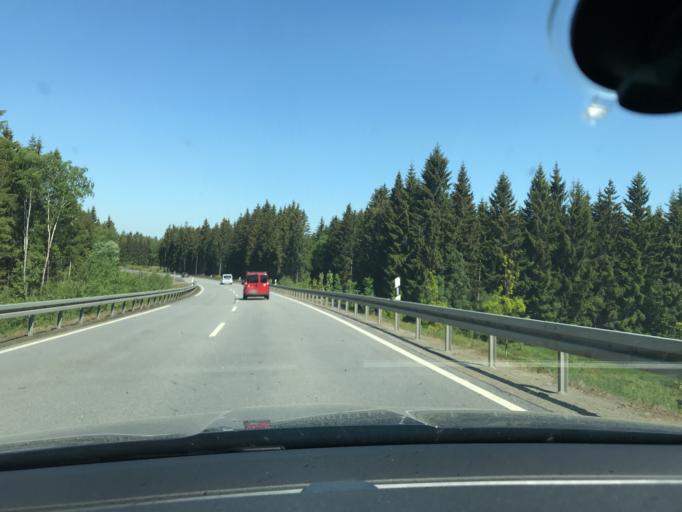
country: DE
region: Saxony
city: Elterlein
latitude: 50.5998
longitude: 12.8573
